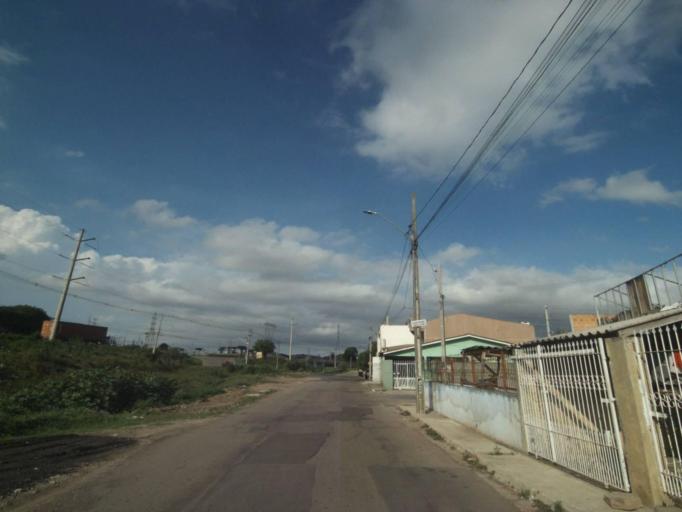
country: BR
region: Parana
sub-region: Araucaria
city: Araucaria
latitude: -25.5257
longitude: -49.3358
